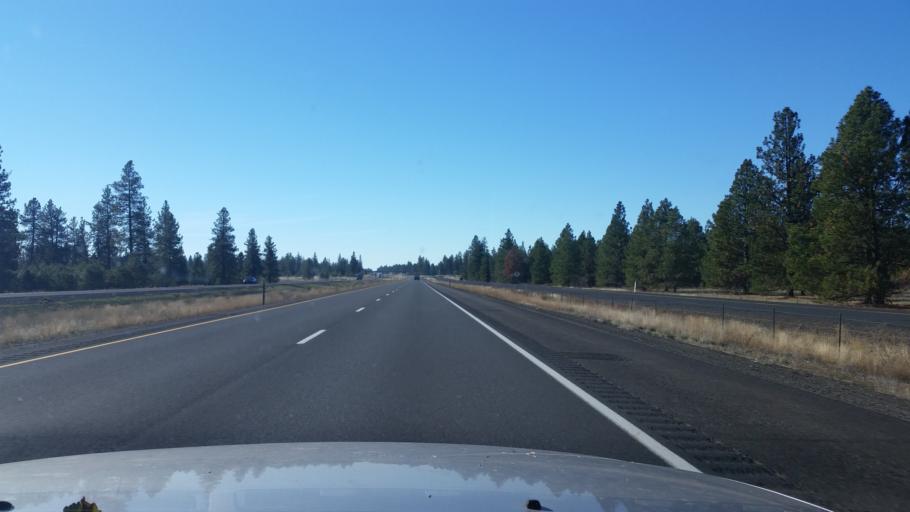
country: US
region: Washington
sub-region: Spokane County
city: Medical Lake
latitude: 47.4437
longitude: -117.7803
